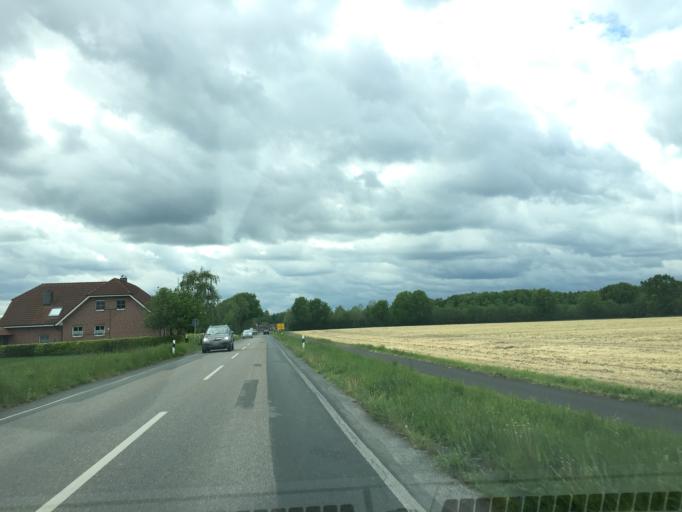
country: DE
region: North Rhine-Westphalia
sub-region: Regierungsbezirk Munster
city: Havixbeck
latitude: 51.9528
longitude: 7.5153
